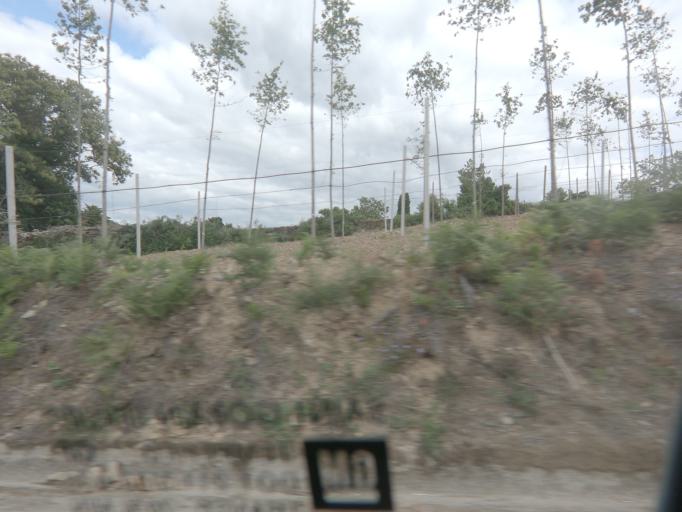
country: PT
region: Vila Real
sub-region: Sabrosa
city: Sabrosa
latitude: 41.2564
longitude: -7.5968
